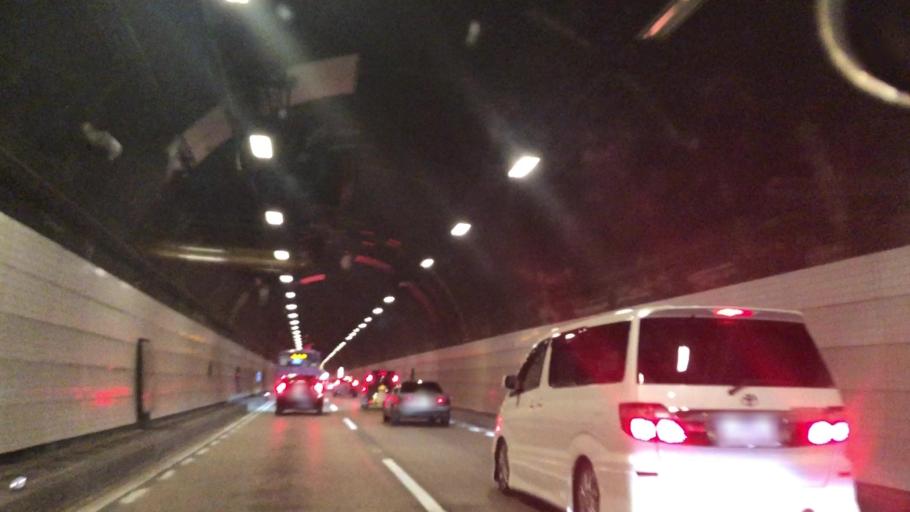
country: JP
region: Miyagi
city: Sendai
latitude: 38.2620
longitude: 140.8404
